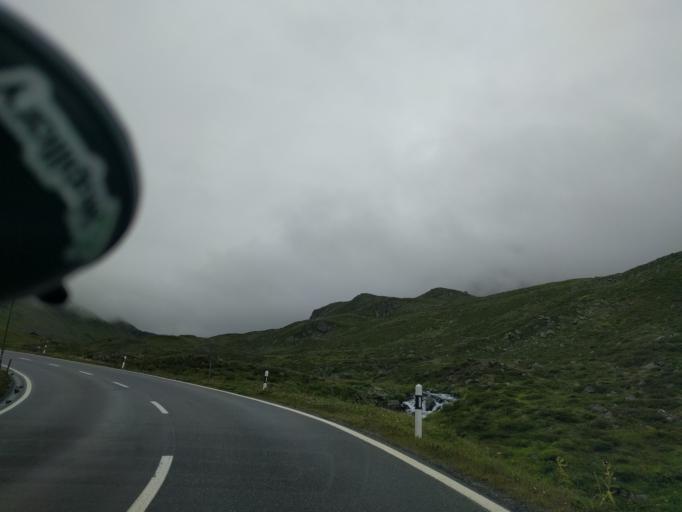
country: CH
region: Grisons
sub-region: Praettigau/Davos District
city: Davos
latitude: 46.7707
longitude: 9.9377
